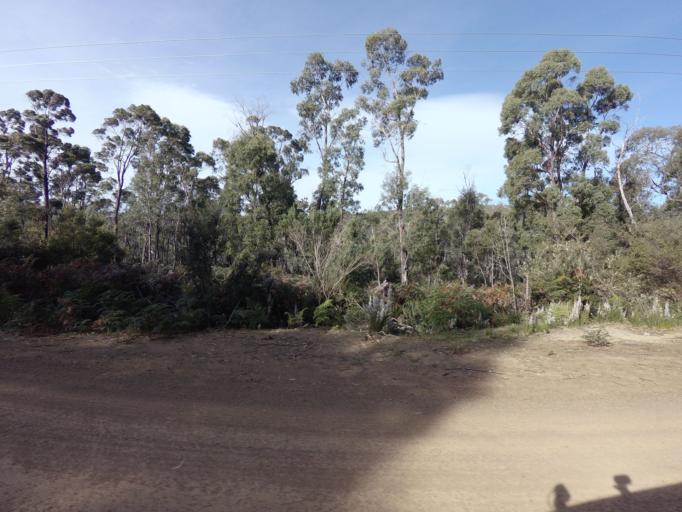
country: AU
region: Tasmania
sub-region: Kingborough
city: Margate
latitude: -43.0788
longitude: 147.2651
